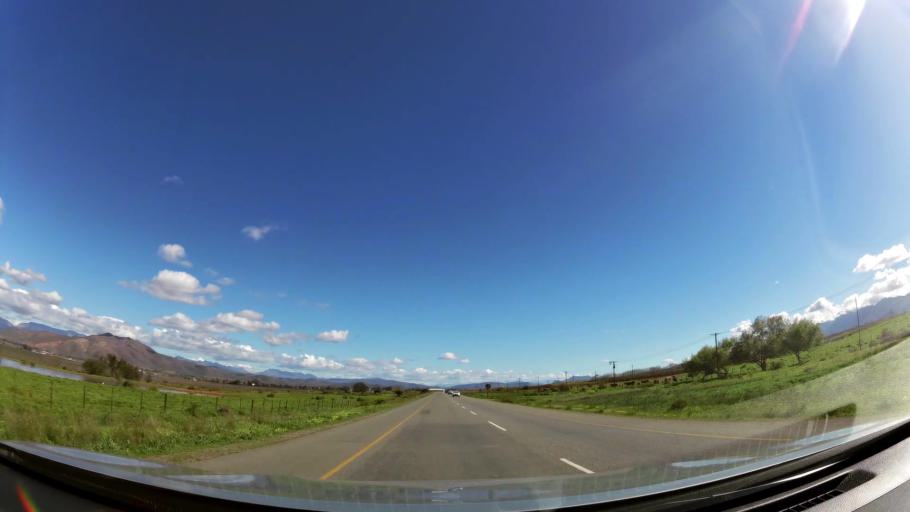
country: ZA
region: Western Cape
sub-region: Cape Winelands District Municipality
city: Ashton
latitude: -33.8385
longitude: 20.0262
